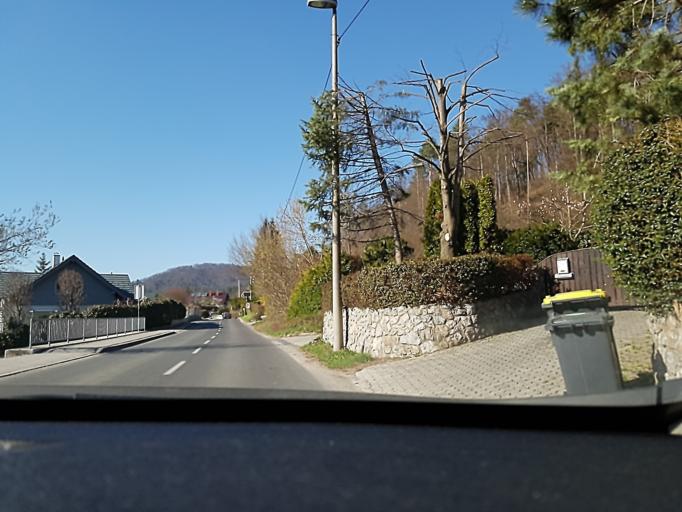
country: SI
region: Trzin
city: Trzin
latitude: 46.1170
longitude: 14.5057
